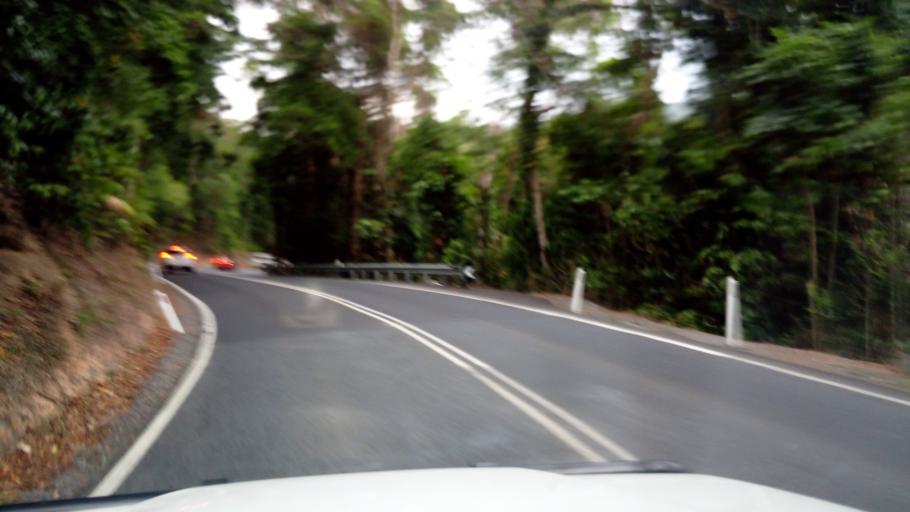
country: AU
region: Queensland
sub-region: Tablelands
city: Kuranda
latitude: -16.8269
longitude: 145.6524
